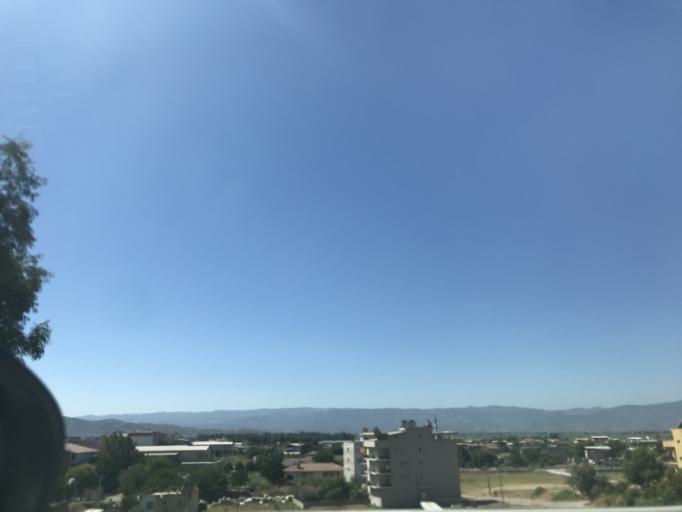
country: TR
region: Aydin
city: Aydin
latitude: 37.8207
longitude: 27.8376
